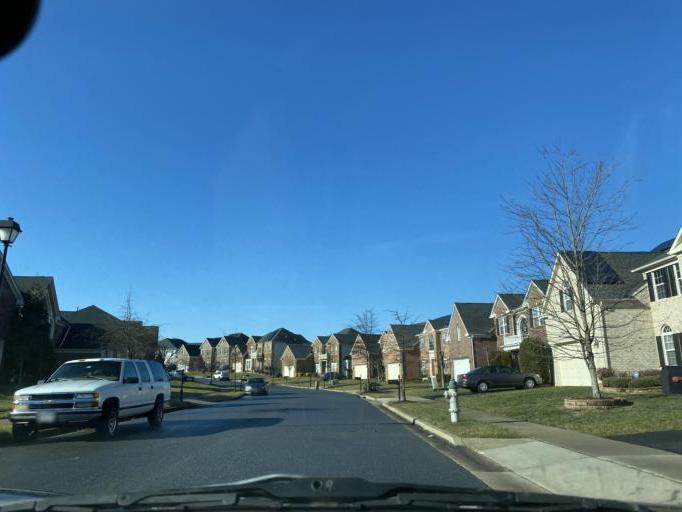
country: US
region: Maryland
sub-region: Prince George's County
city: West Laurel
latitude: 39.0902
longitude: -76.8805
